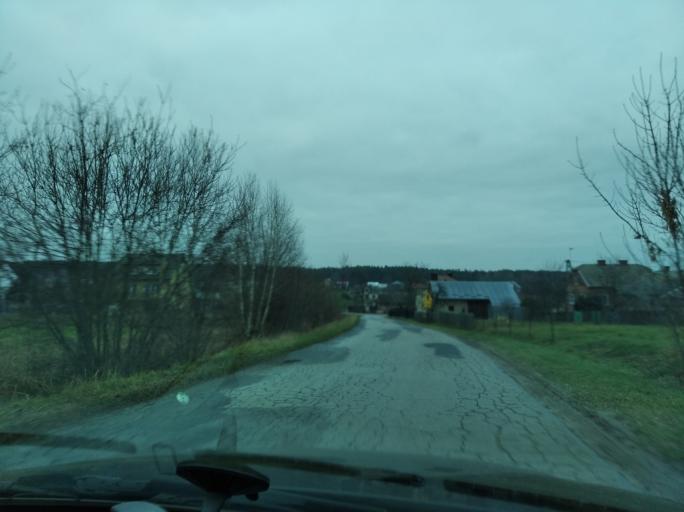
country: PL
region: Subcarpathian Voivodeship
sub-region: Powiat lancucki
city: Brzoza Stadnicka
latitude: 50.1900
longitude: 22.2570
